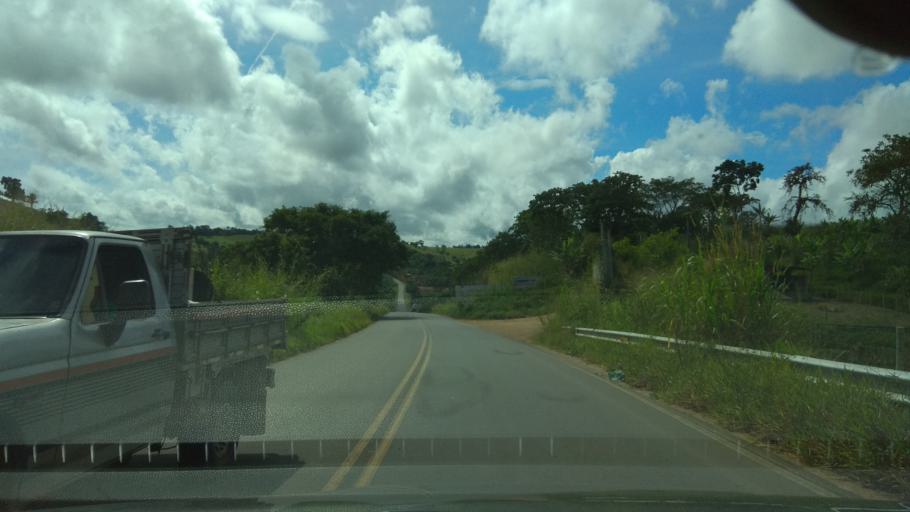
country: BR
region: Bahia
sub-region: Mutuipe
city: Mutuipe
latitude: -13.2286
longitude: -39.4924
